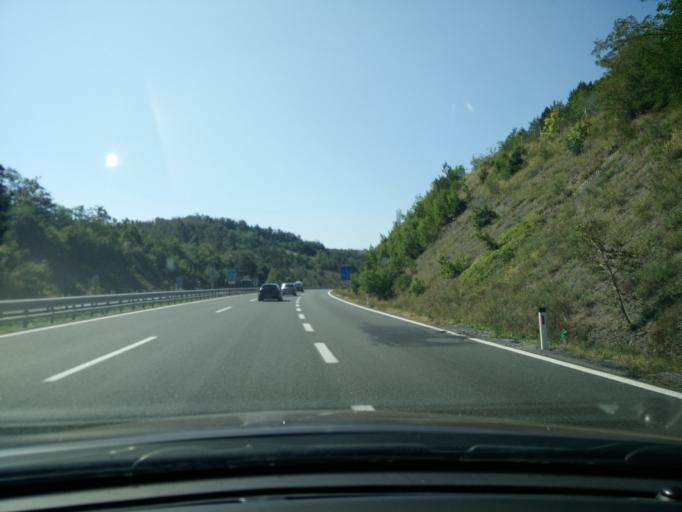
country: SI
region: Divaca
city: Divaca
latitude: 45.7471
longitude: 14.0416
